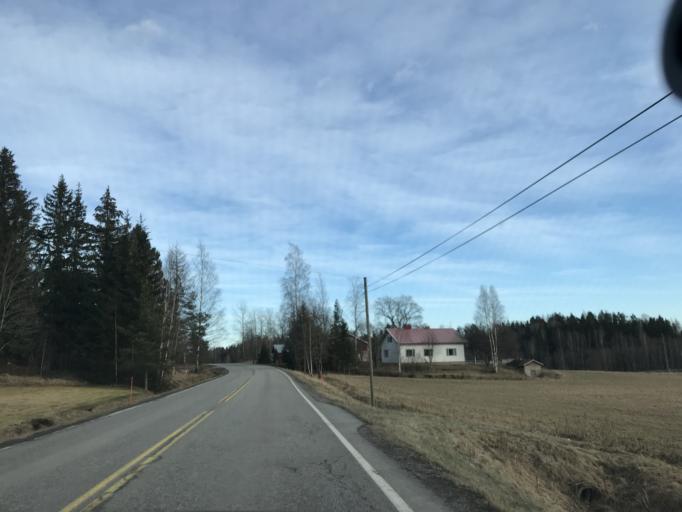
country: FI
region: Uusimaa
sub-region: Raaseporin
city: Pohja
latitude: 60.0930
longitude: 23.4704
